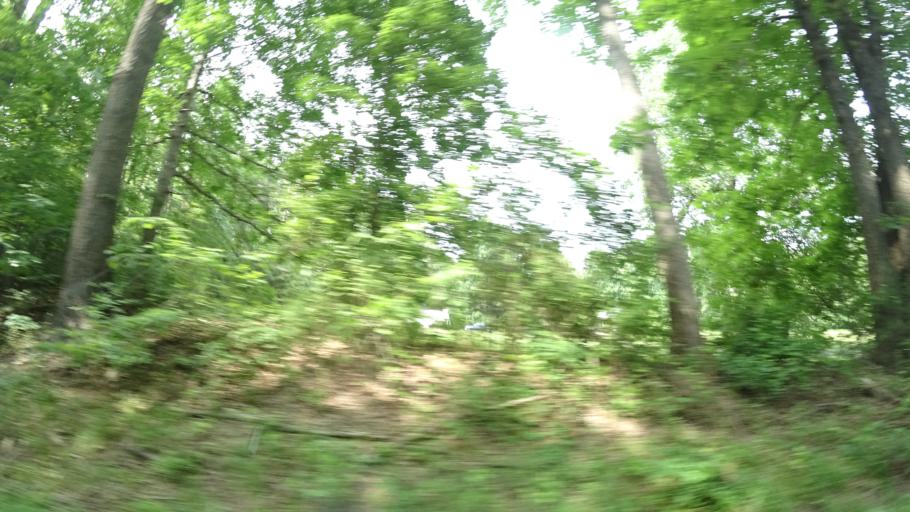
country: US
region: Virginia
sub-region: Spotsylvania County
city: Spotsylvania Courthouse
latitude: 38.1569
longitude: -77.6337
